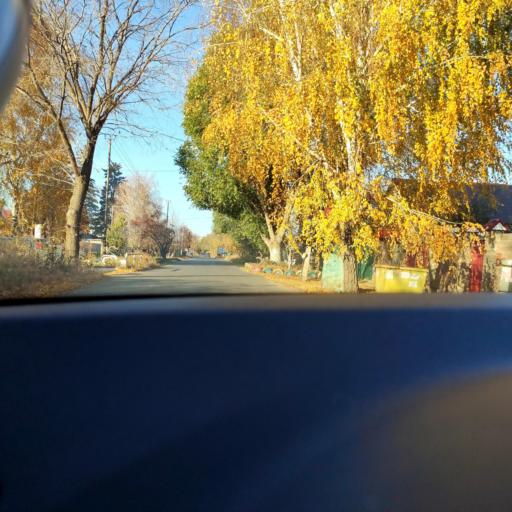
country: RU
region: Samara
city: Petra-Dubrava
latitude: 53.2455
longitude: 50.3279
